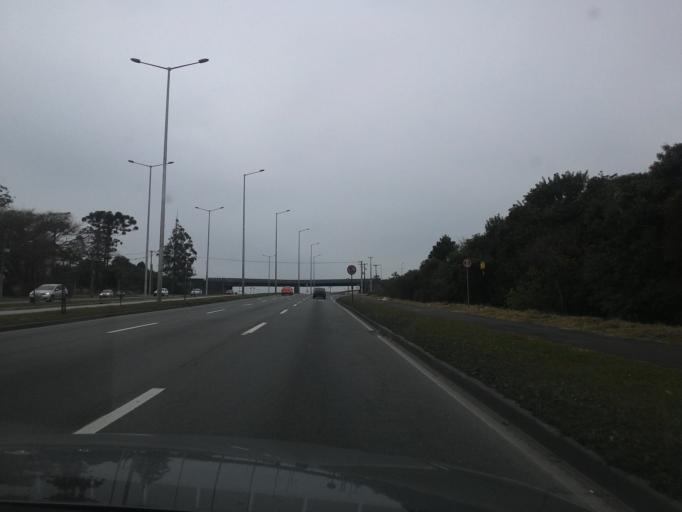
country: BR
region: Parana
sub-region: Pinhais
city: Pinhais
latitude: -25.4460
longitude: -49.2345
